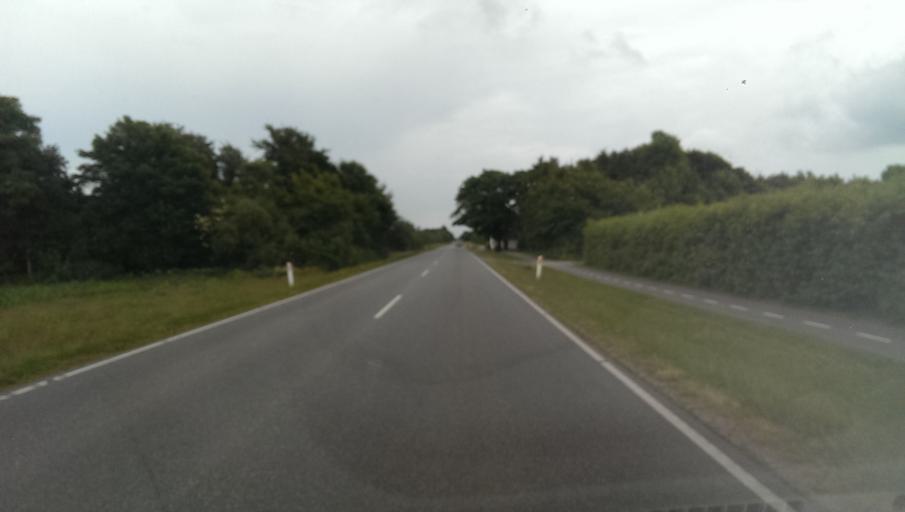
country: DK
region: South Denmark
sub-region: Esbjerg Kommune
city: Bramming
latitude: 55.4584
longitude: 8.7123
